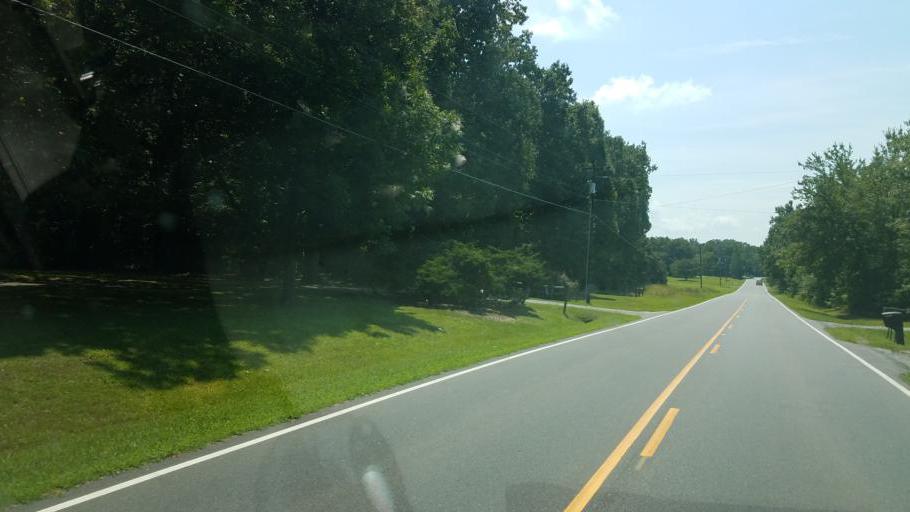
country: US
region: North Carolina
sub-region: Gaston County
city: Cherryville
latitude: 35.3628
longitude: -81.3638
